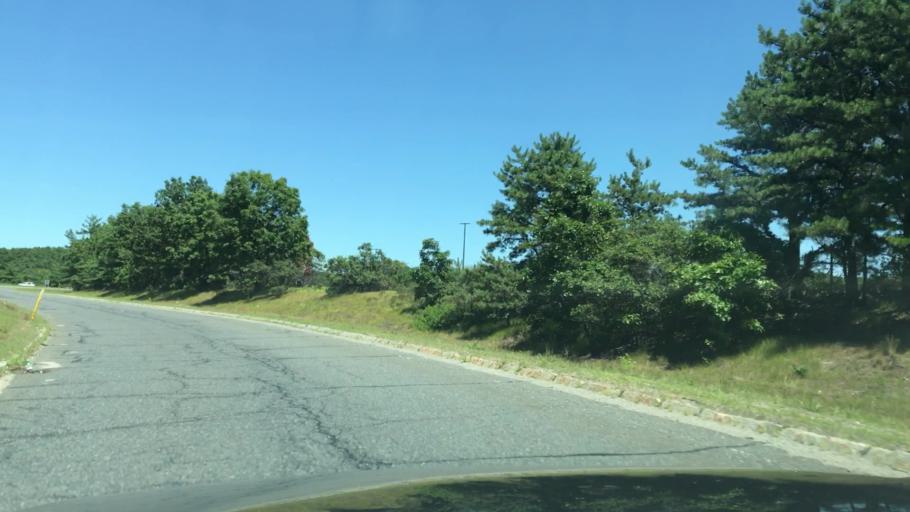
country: US
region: Massachusetts
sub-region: Bristol County
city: North Seekonk
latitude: 41.9013
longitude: -71.3537
